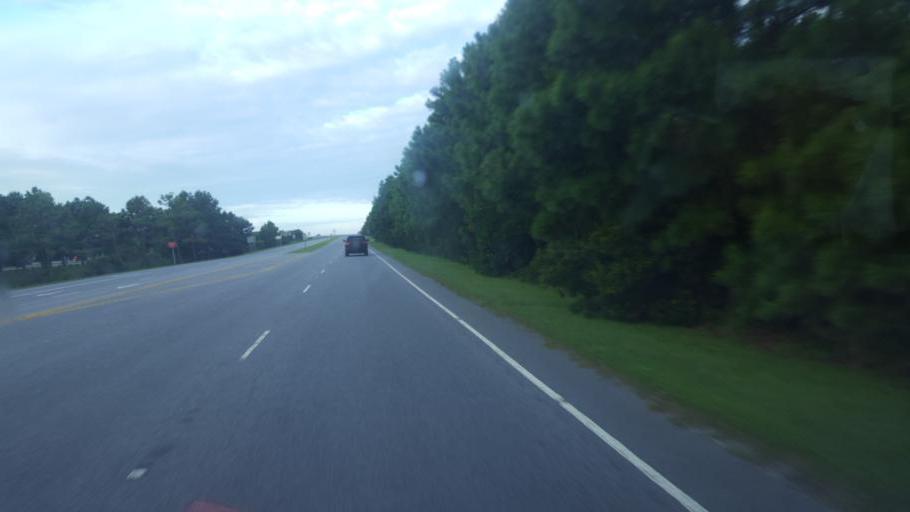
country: US
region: North Carolina
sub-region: Dare County
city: Manteo
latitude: 35.8877
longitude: -75.6666
